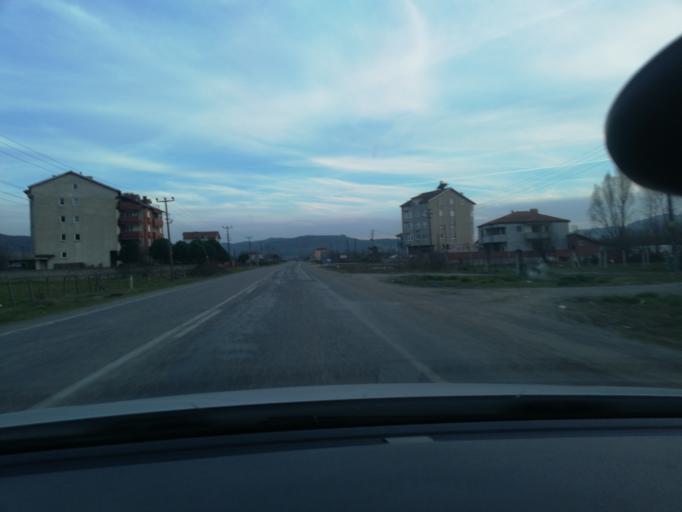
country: TR
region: Zonguldak
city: Saltukova
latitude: 41.5245
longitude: 32.1007
